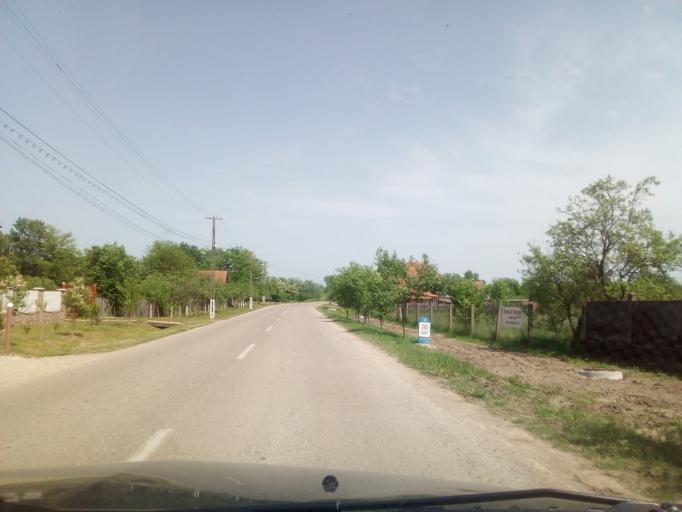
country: RO
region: Timis
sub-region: Comuna Balint
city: Balint
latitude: 45.8157
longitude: 21.8609
